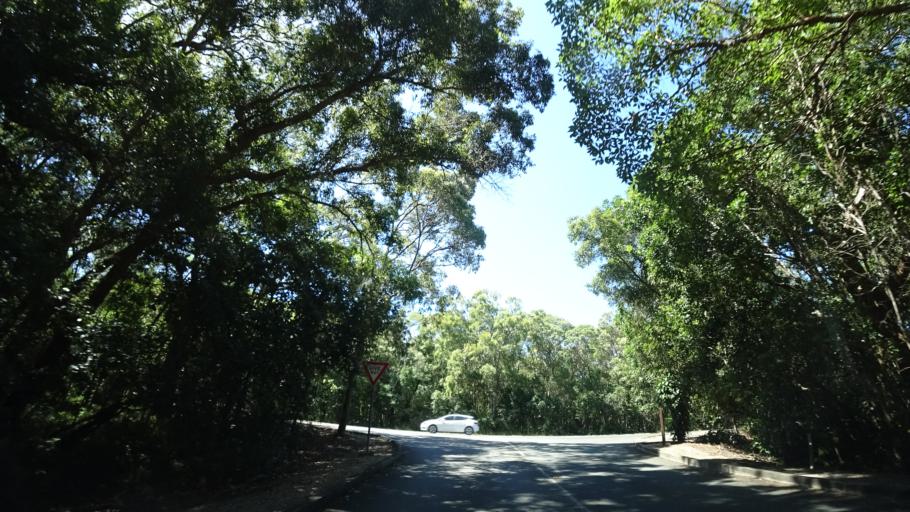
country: AU
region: Queensland
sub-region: Sunshine Coast
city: Mooloolaba
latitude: -26.6310
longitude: 153.0965
